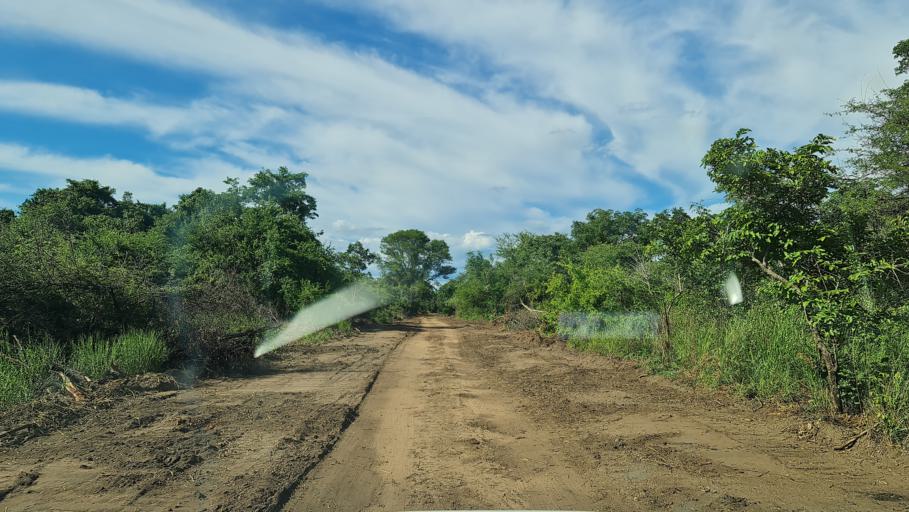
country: MZ
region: Nampula
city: Antonio Enes
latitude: -15.5249
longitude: 40.1270
